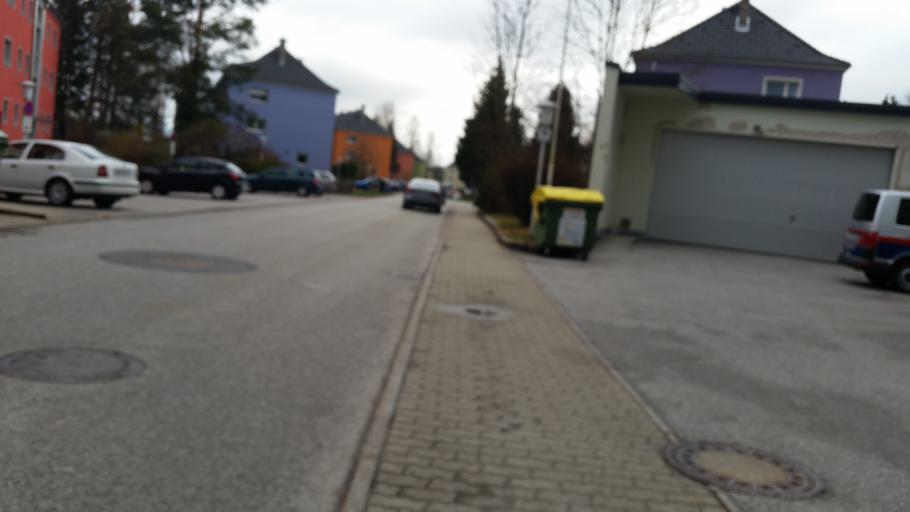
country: DE
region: Bavaria
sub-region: Upper Bavaria
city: Ainring
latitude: 47.7900
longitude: 12.9774
